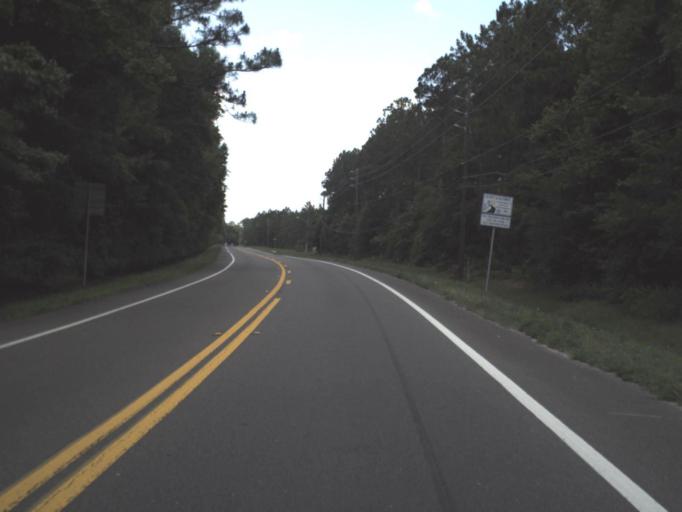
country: US
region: Florida
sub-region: Nassau County
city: Nassau Village-Ratliff
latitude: 30.4857
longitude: -81.7227
